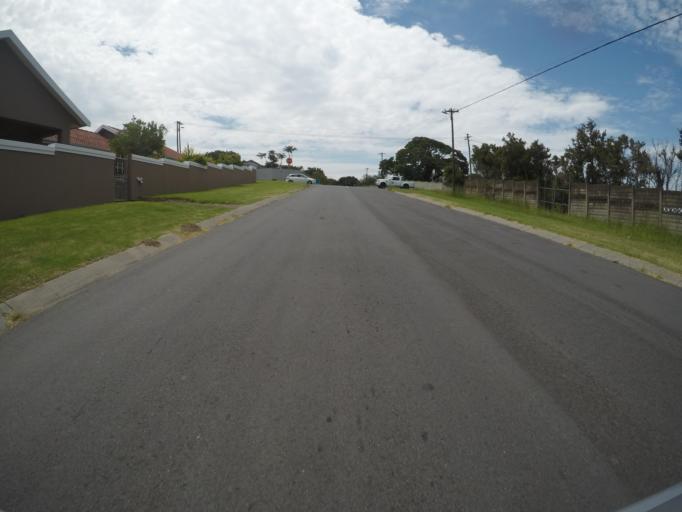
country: ZA
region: Eastern Cape
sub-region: Buffalo City Metropolitan Municipality
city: East London
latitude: -32.9886
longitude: 27.8674
